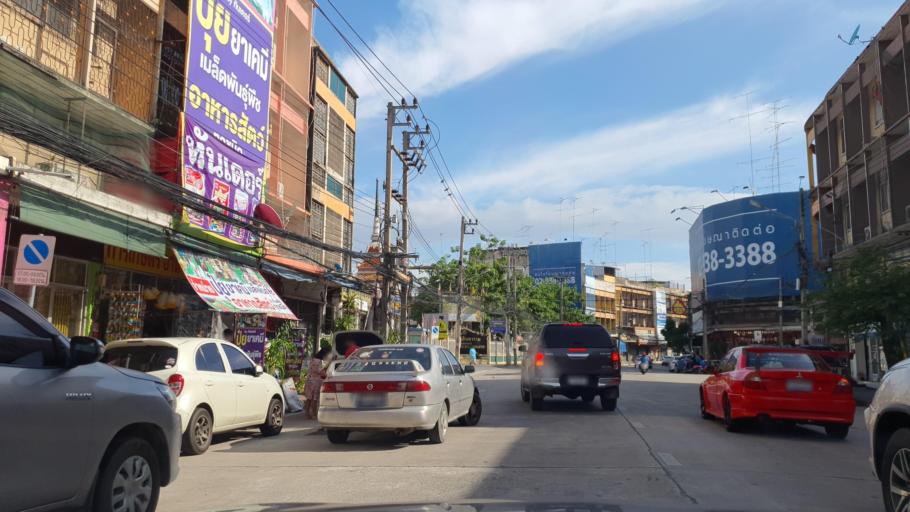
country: TH
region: Chon Buri
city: Chon Buri
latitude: 13.3644
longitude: 100.9875
